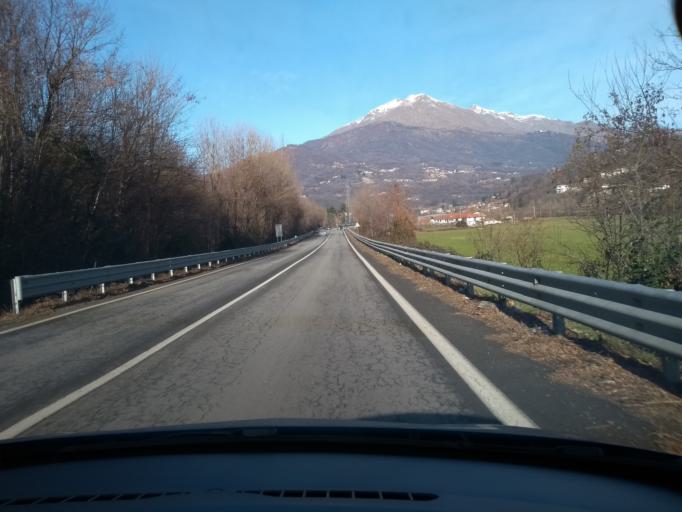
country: IT
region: Piedmont
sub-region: Provincia di Torino
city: Cuorgne
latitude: 45.3872
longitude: 7.6617
